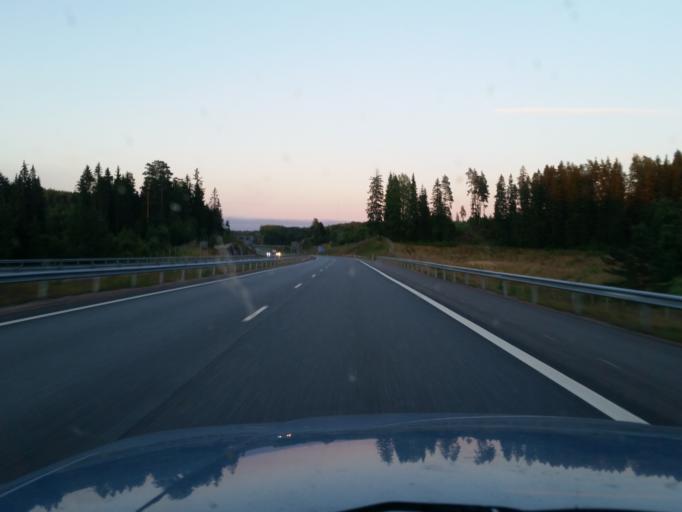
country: FI
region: Uusimaa
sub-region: Helsinki
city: Sammatti
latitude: 60.3801
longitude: 23.7878
